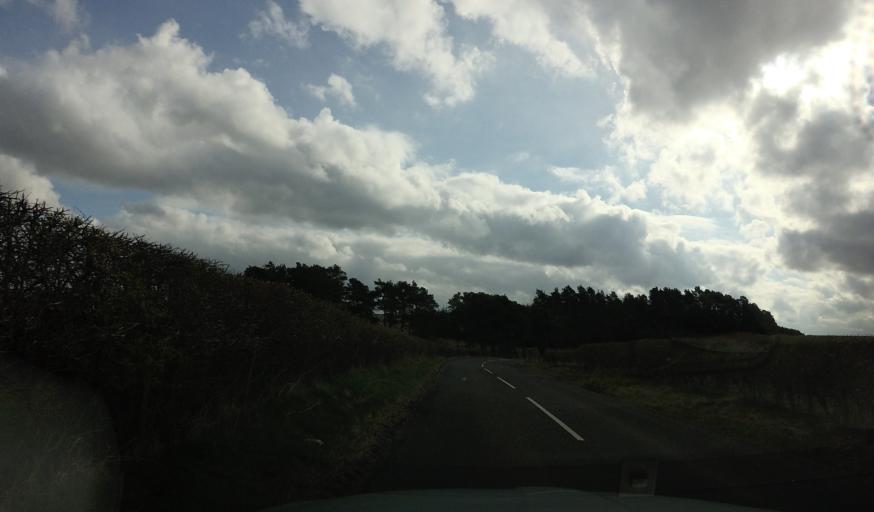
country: GB
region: Scotland
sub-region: Midlothian
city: Loanhead
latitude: 55.7959
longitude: -3.1472
